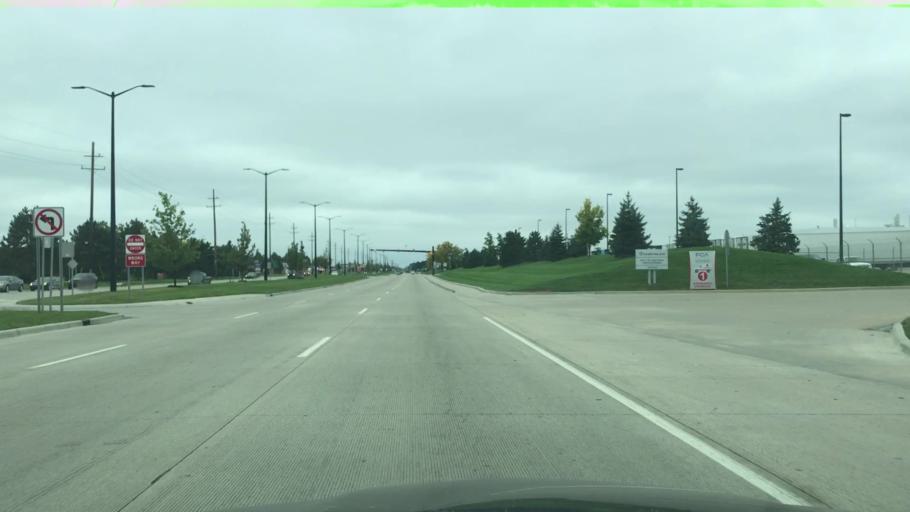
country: US
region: Michigan
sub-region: Macomb County
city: Sterling Heights
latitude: 42.5781
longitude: -83.0304
